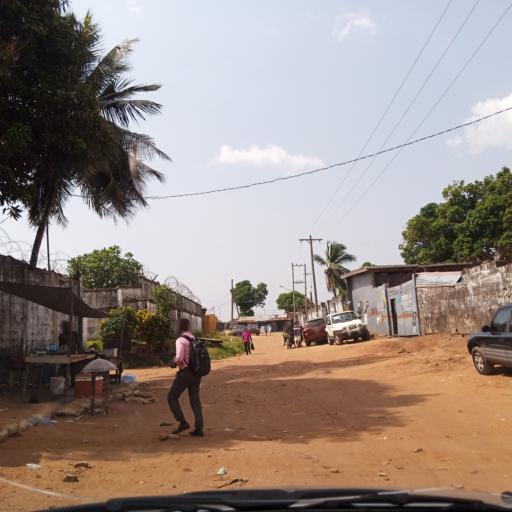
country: LR
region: Montserrado
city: Monrovia
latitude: 6.2901
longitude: -10.7654
